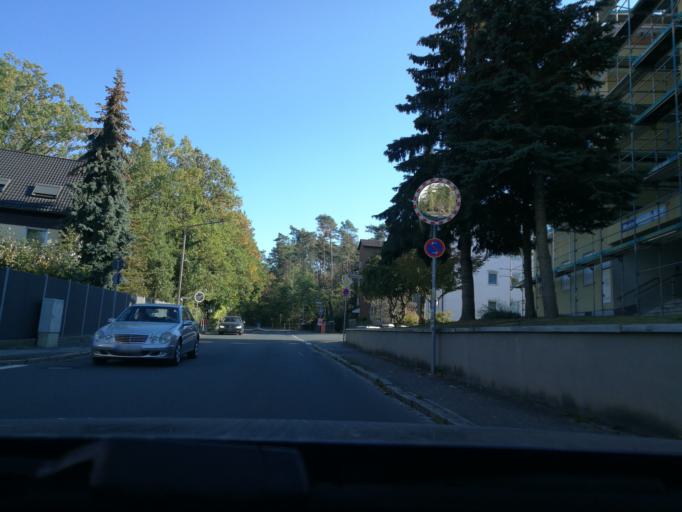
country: DE
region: Bavaria
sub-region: Regierungsbezirk Mittelfranken
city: Zirndorf
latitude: 49.4570
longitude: 10.9326
